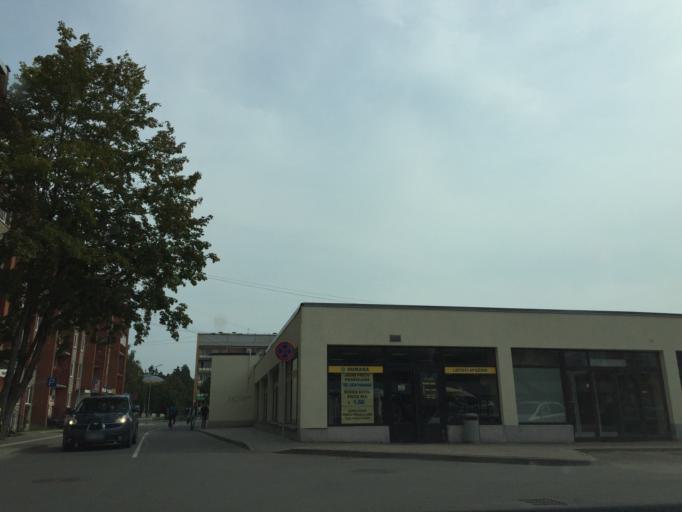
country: LV
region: Ogre
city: Ogre
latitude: 56.8226
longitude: 24.5946
